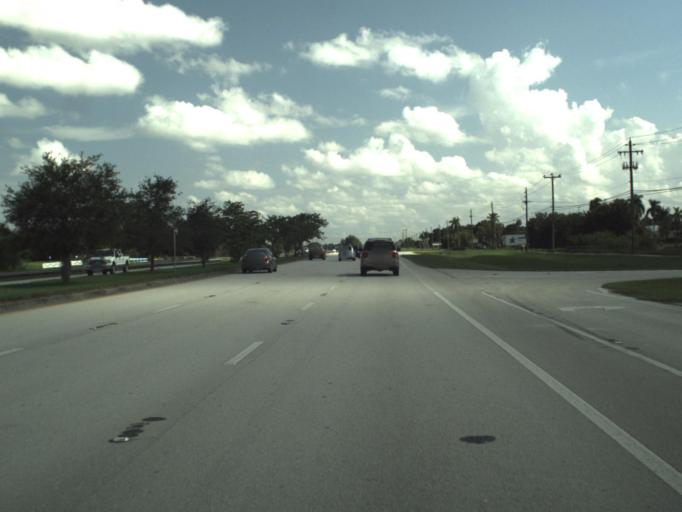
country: US
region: Florida
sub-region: Palm Beach County
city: Greenacres City
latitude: 26.5563
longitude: -80.2059
